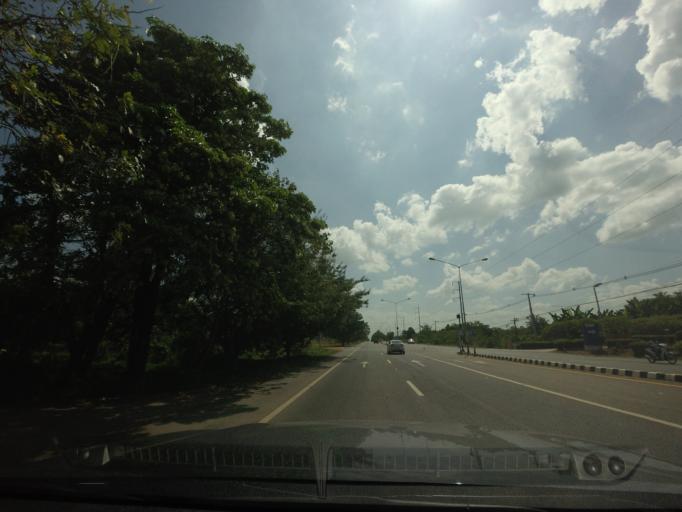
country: TH
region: Phetchabun
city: Nong Phai
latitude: 16.0216
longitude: 101.0736
